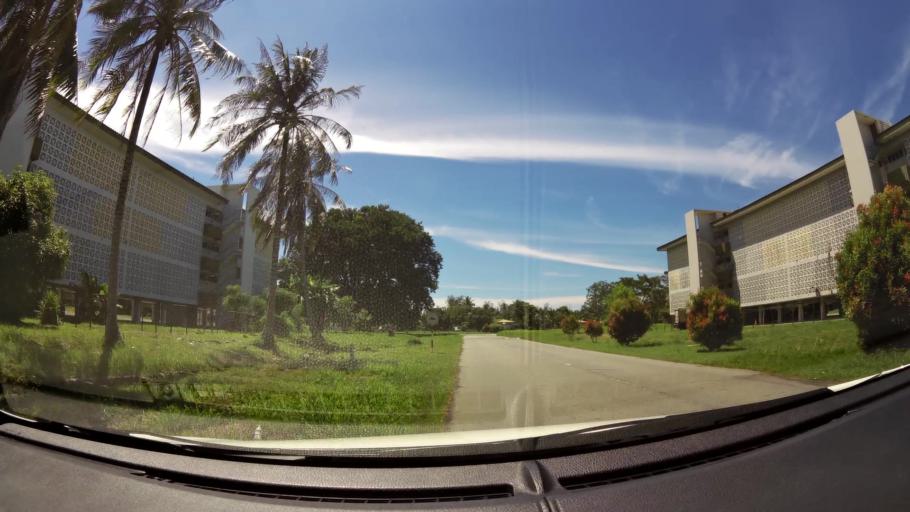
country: BN
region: Brunei and Muara
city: Bandar Seri Begawan
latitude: 5.0337
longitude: 115.0672
